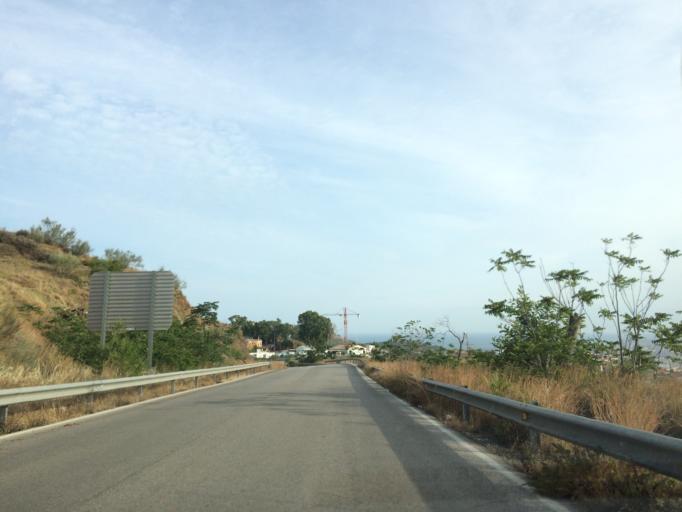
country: ES
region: Andalusia
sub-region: Provincia de Malaga
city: Malaga
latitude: 36.7517
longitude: -4.4082
